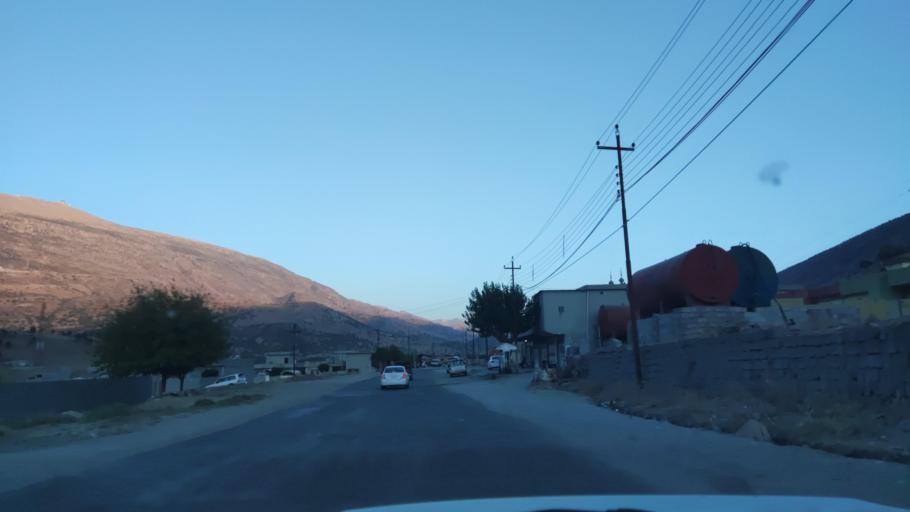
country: IQ
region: Arbil
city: Ruwandiz
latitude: 36.5888
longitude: 44.3924
